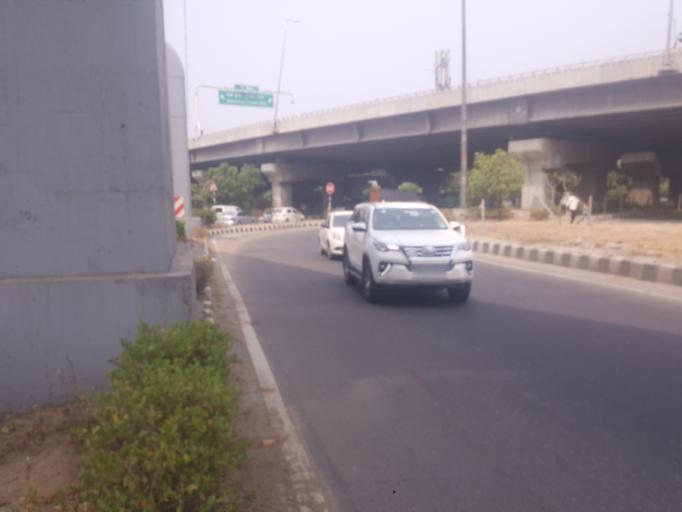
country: IN
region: NCT
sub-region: Central Delhi
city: Karol Bagh
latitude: 28.5702
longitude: 77.1340
